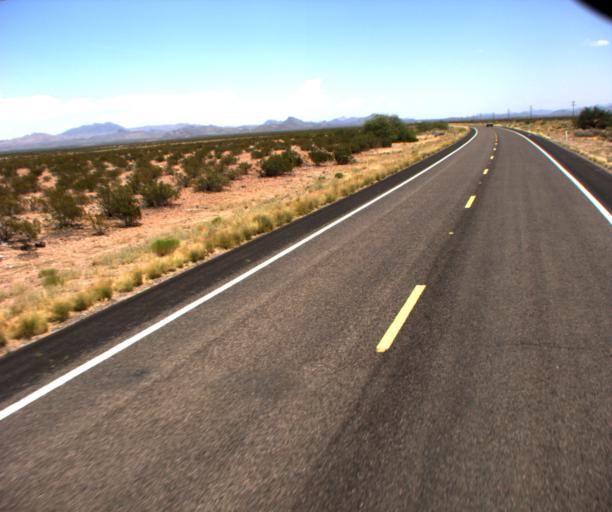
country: US
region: Arizona
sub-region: Graham County
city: Safford
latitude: 32.7825
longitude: -109.5359
